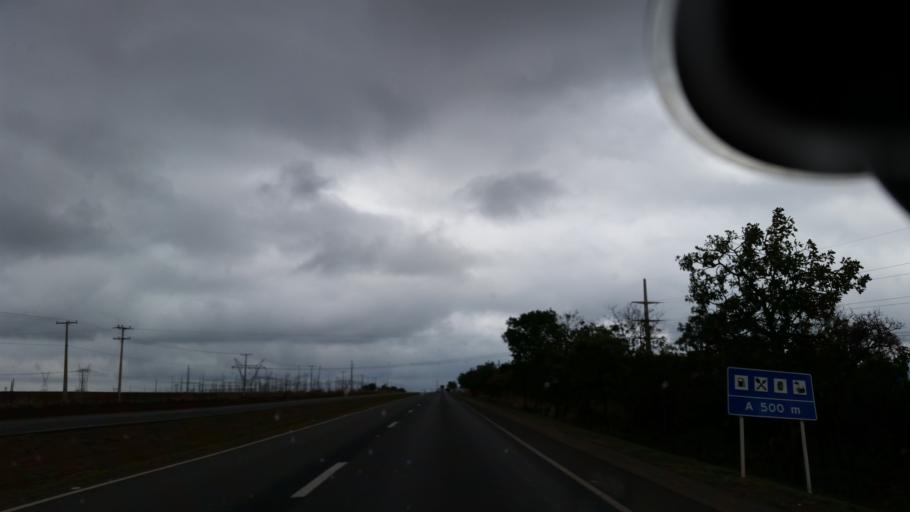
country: BR
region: Goias
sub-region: Luziania
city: Luziania
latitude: -16.3376
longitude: -47.8367
